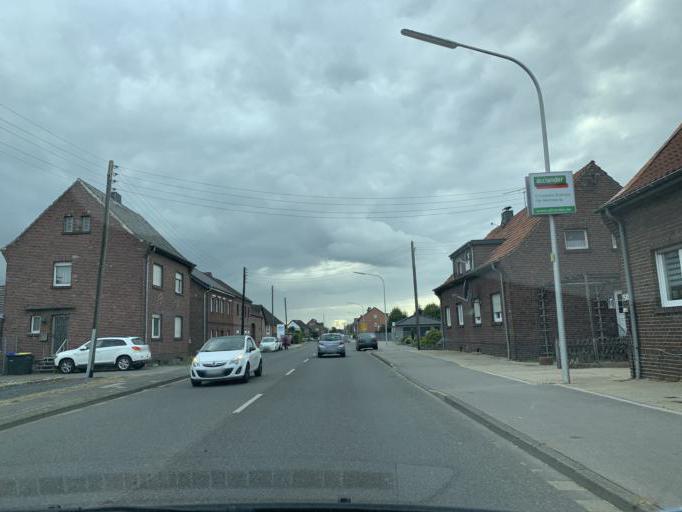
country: DE
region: North Rhine-Westphalia
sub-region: Regierungsbezirk Koln
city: Wassenberg
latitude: 51.0777
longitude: 6.1354
